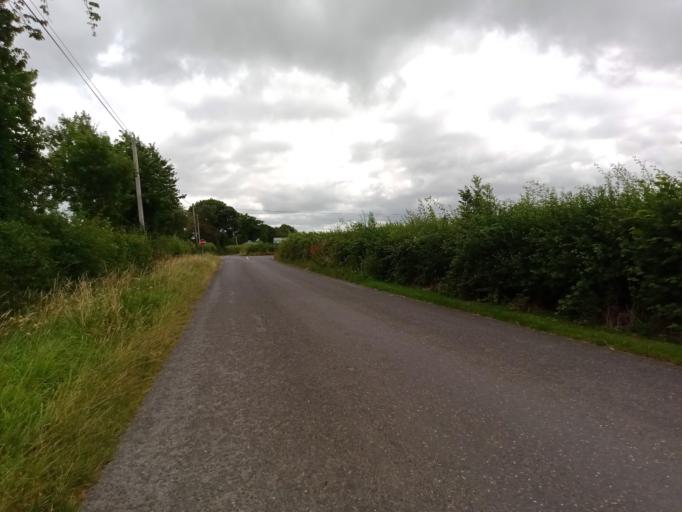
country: IE
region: Leinster
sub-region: Kilkenny
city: Callan
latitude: 52.5763
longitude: -7.3784
